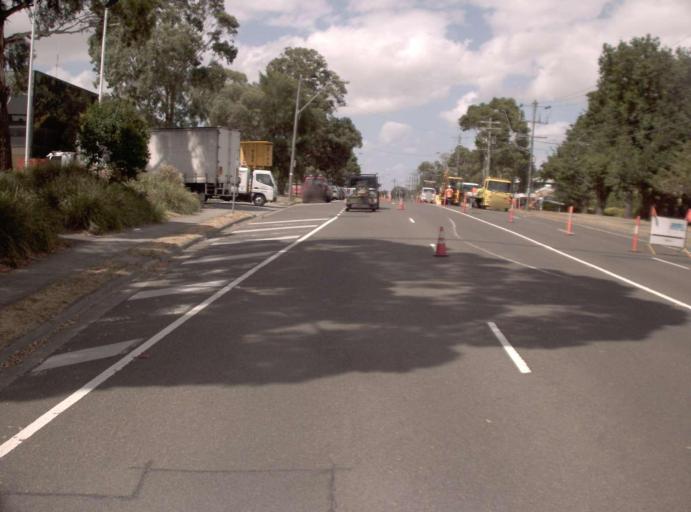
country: AU
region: Victoria
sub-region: Monash
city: Notting Hill
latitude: -37.8961
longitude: 145.1299
